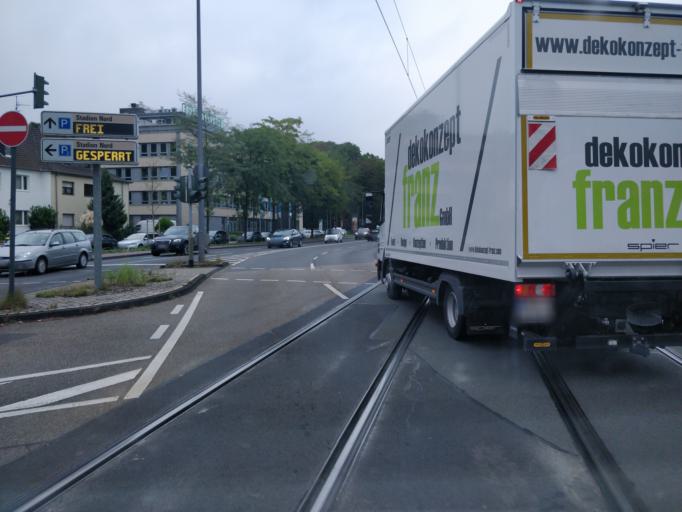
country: DE
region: North Rhine-Westphalia
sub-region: Regierungsbezirk Koln
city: Mengenich
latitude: 50.9384
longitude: 6.8634
